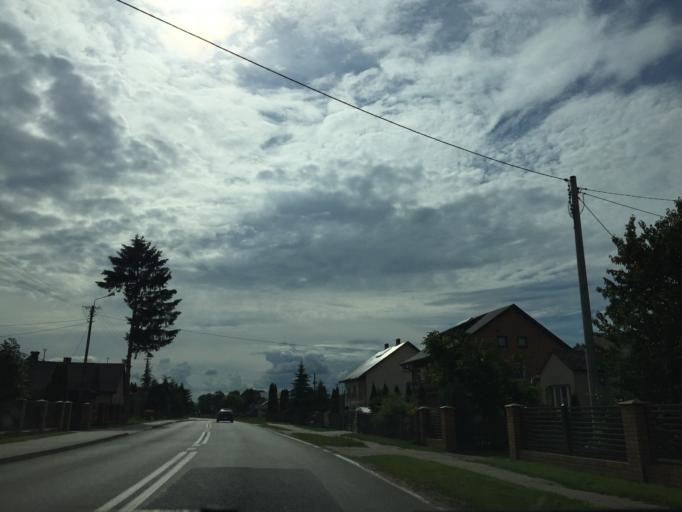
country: PL
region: Lublin Voivodeship
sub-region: Powiat lukowski
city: Trzebieszow
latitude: 51.9896
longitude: 22.5526
